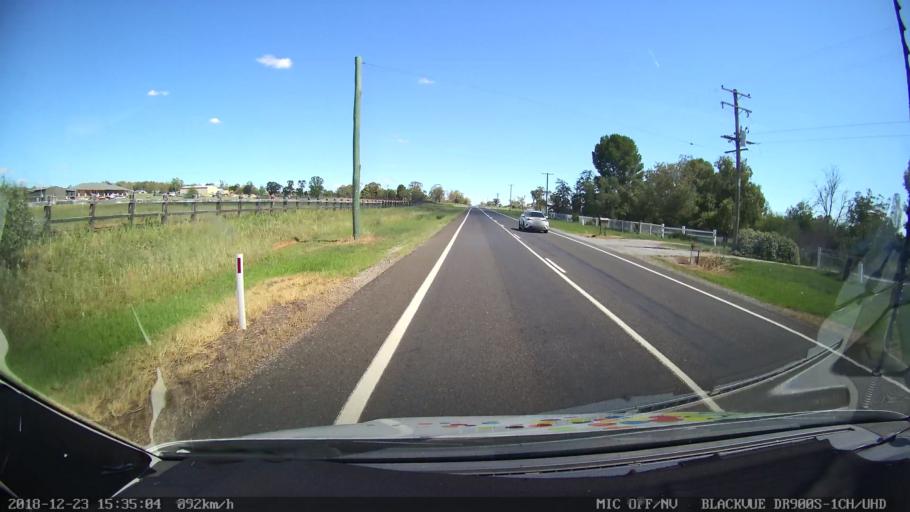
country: AU
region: New South Wales
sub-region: Tamworth Municipality
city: Tamworth
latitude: -31.0224
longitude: 150.8810
